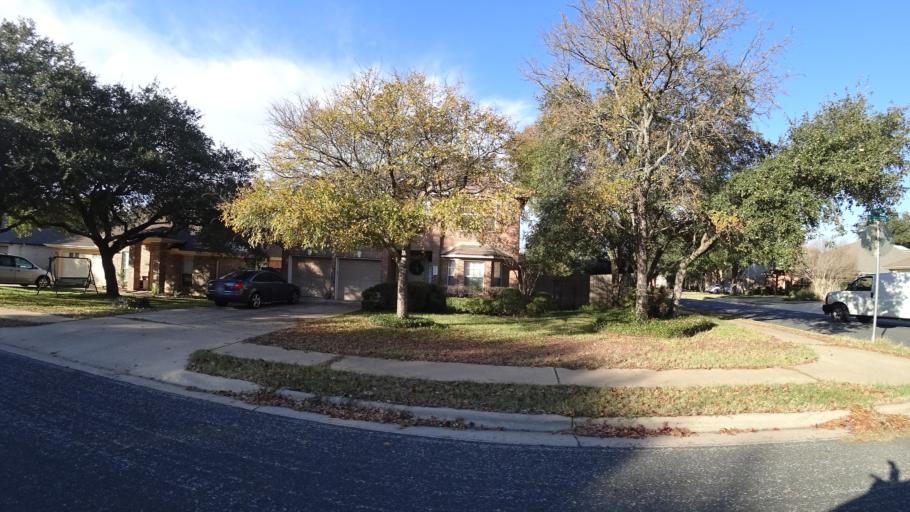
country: US
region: Texas
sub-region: Williamson County
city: Brushy Creek
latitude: 30.5034
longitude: -97.7417
